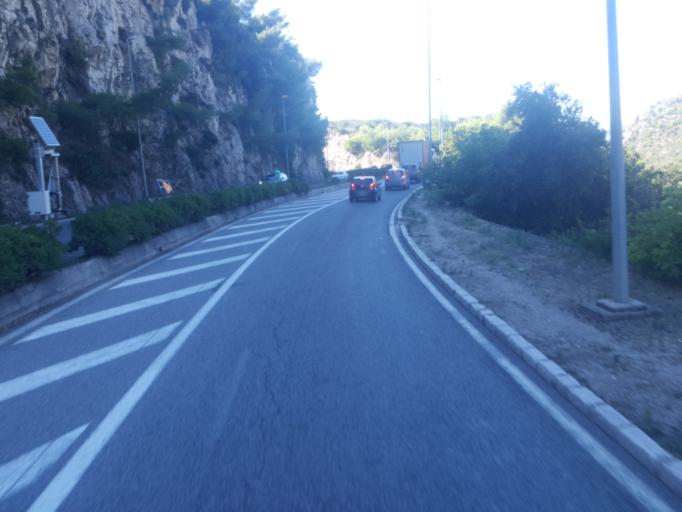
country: FR
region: Provence-Alpes-Cote d'Azur
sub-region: Departement des Alpes-Maritimes
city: Cap-d'Ail
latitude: 43.7277
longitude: 7.3902
